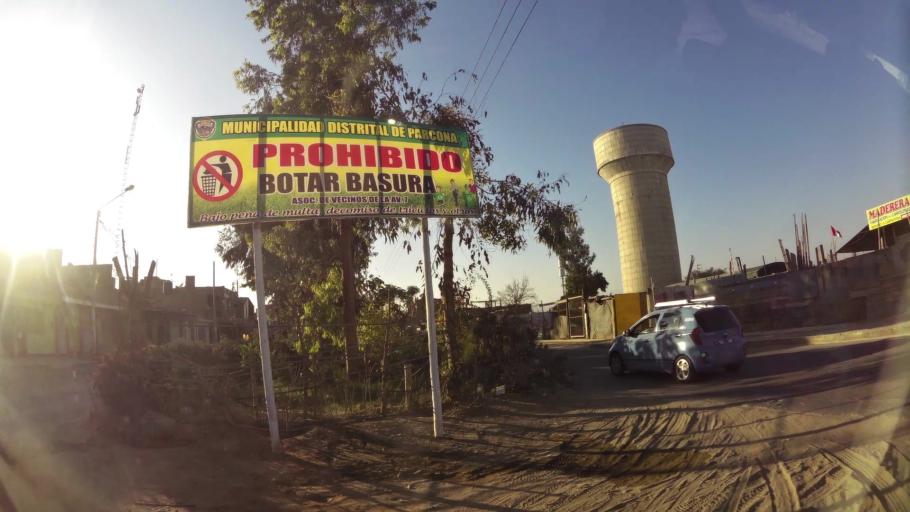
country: PE
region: Ica
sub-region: Provincia de Ica
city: Ica
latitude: -14.0645
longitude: -75.7203
